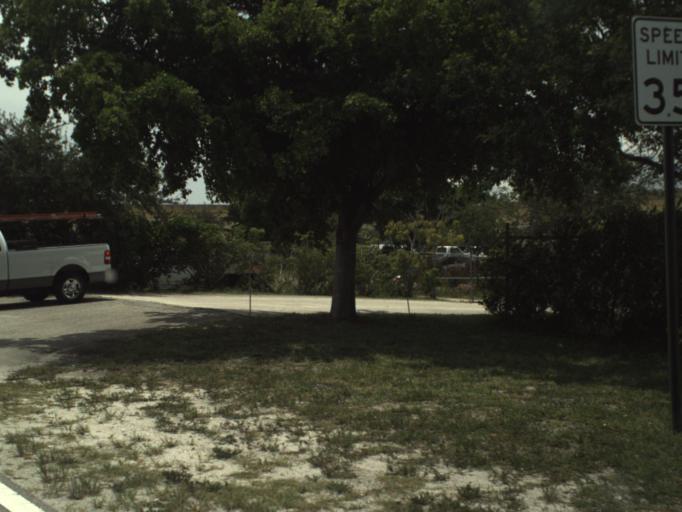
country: US
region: Florida
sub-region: Palm Beach County
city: Lake Worth
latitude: 26.6240
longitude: -80.0750
